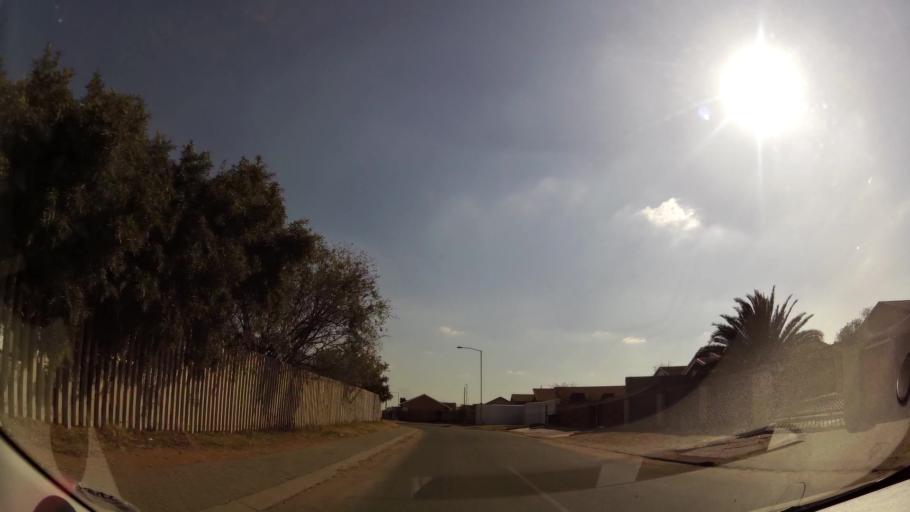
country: ZA
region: Gauteng
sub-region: City of Johannesburg Metropolitan Municipality
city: Roodepoort
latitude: -26.1684
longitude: 27.7988
